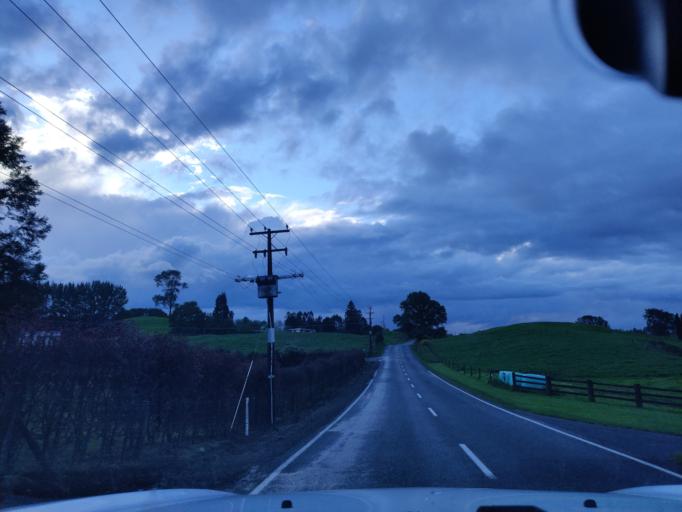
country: NZ
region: Waikato
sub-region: South Waikato District
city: Tokoroa
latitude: -38.2139
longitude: 175.8276
